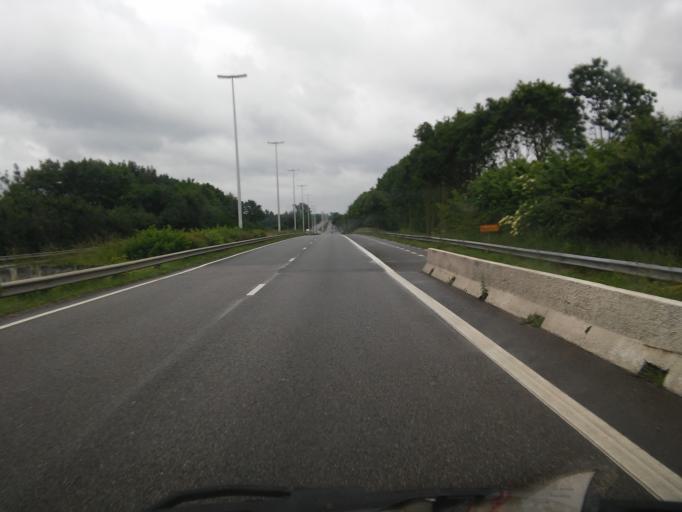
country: BE
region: Flanders
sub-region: Provincie Oost-Vlaanderen
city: Aalst
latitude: 50.9055
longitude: 4.0323
